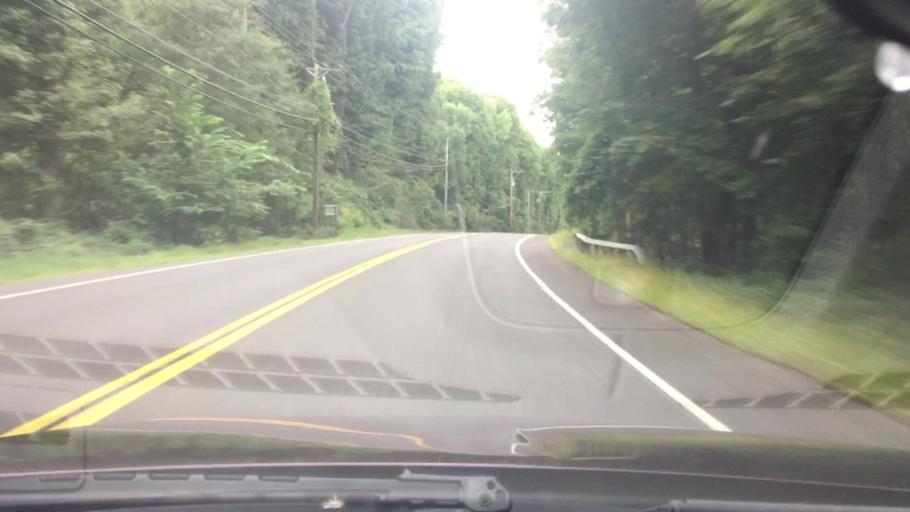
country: US
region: New York
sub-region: Dutchess County
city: Millbrook
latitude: 41.7797
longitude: -73.7413
